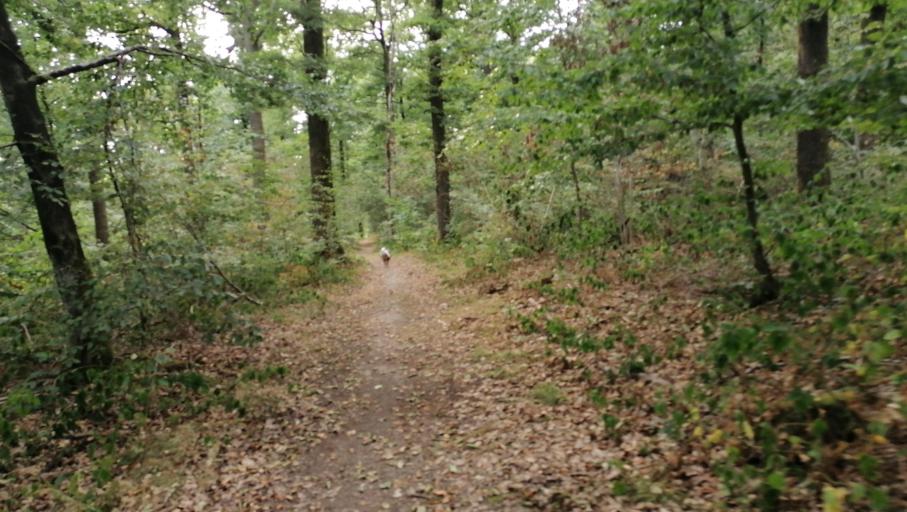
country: BE
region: Wallonia
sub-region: Province du Hainaut
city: Beaumont
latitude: 50.2201
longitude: 4.1542
